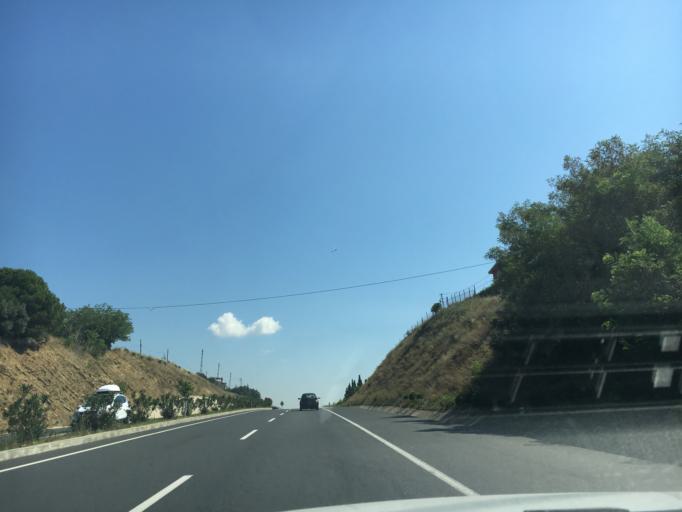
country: TR
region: Tekirdag
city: Sultankoy
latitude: 41.0225
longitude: 27.9950
